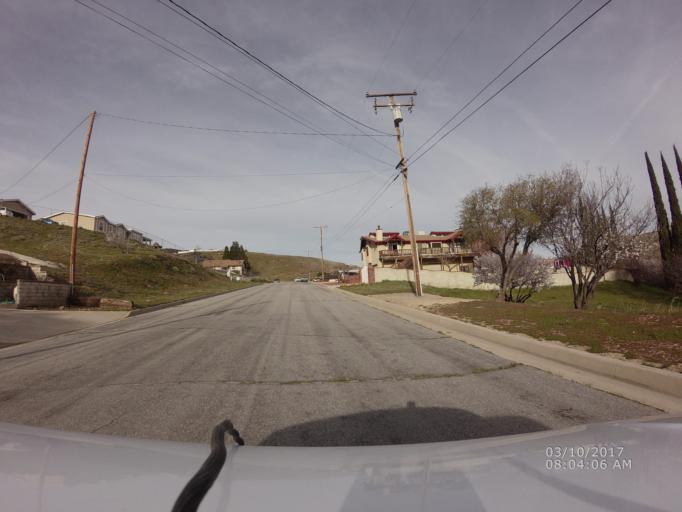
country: US
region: California
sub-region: Los Angeles County
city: Green Valley
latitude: 34.6600
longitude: -118.4022
